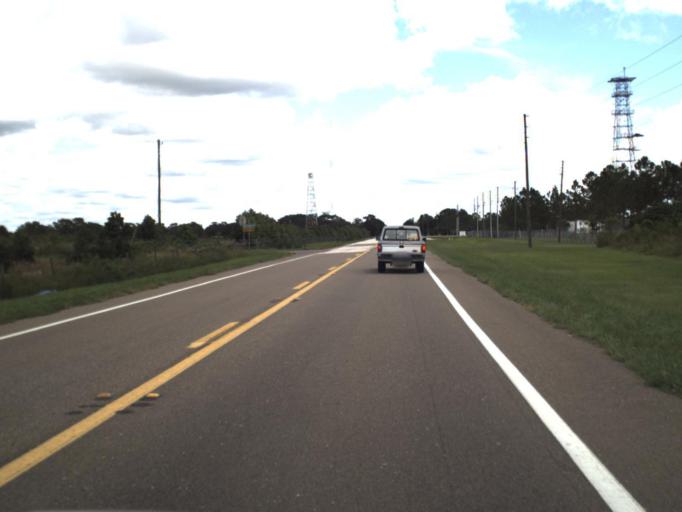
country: US
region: Florida
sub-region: Polk County
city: Frostproof
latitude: 27.7336
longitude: -81.5979
